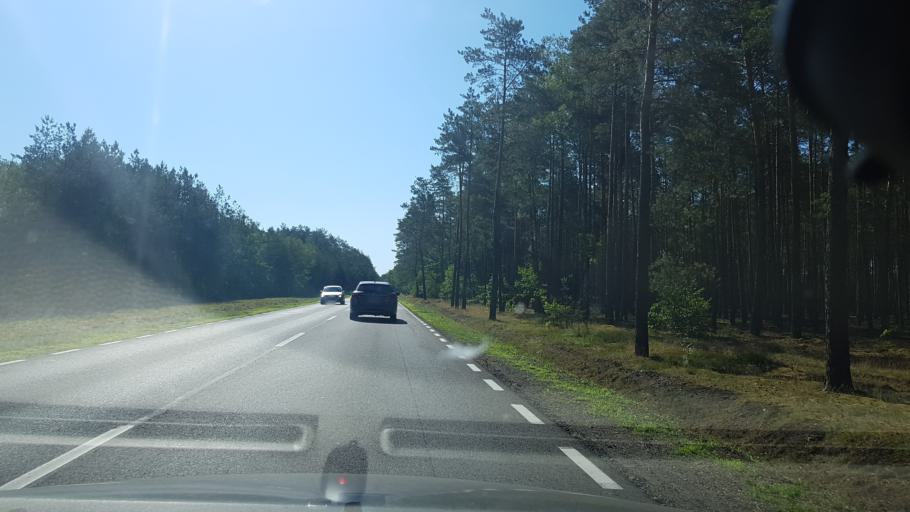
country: PL
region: Masovian Voivodeship
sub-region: Powiat wyszkowski
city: Branszczyk
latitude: 52.5605
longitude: 21.5743
